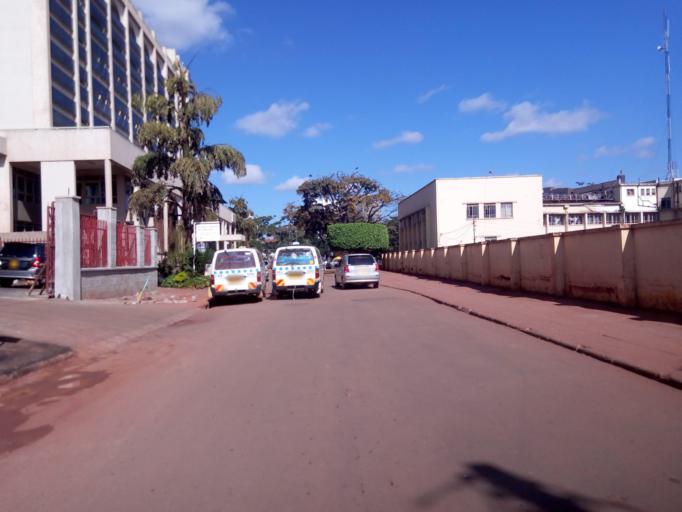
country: UG
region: Central Region
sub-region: Kampala District
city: Kampala
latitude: 0.3168
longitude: 32.5781
